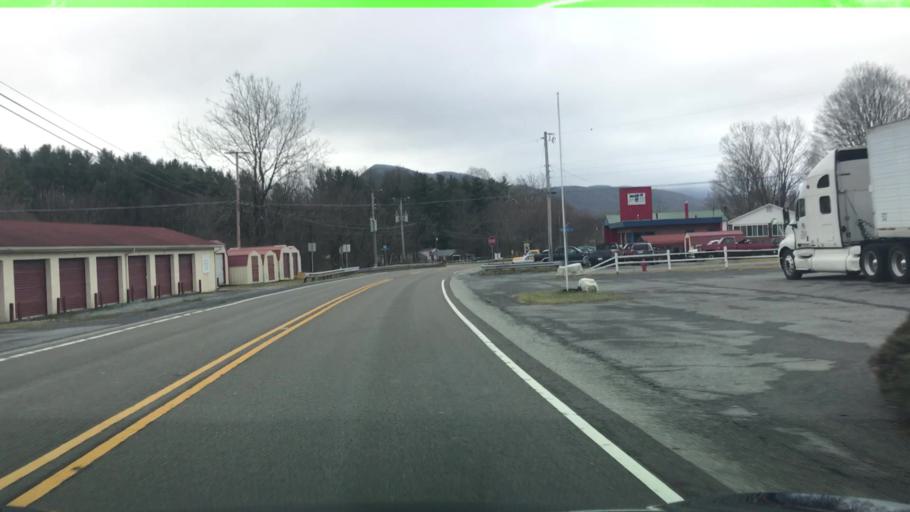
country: US
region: Virginia
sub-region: Smyth County
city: Atkins
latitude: 36.7788
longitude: -81.4082
